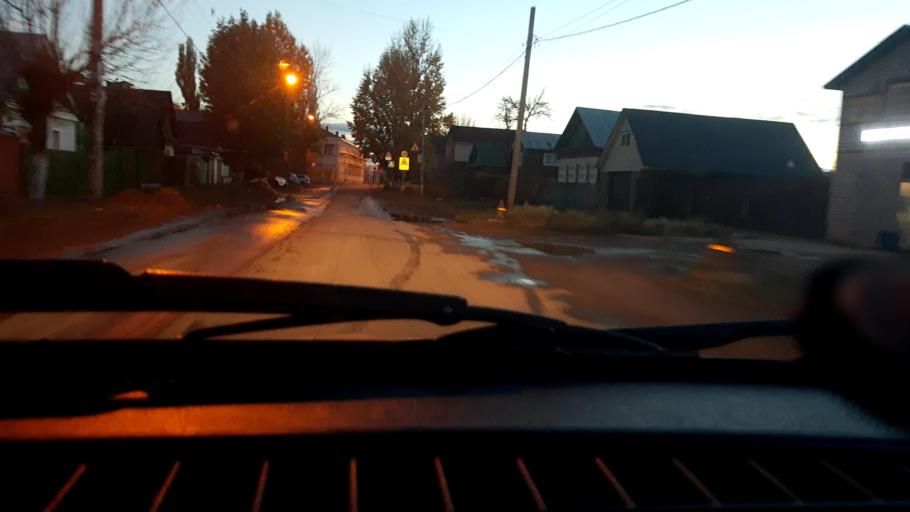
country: RU
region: Bashkortostan
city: Ufa
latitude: 54.7433
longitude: 55.9138
